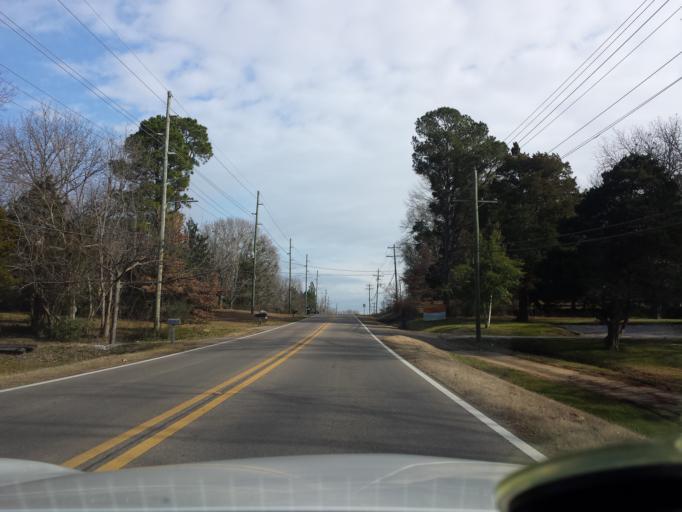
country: US
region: Mississippi
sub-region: Oktibbeha County
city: Starkville
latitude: 33.4643
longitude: -88.8305
